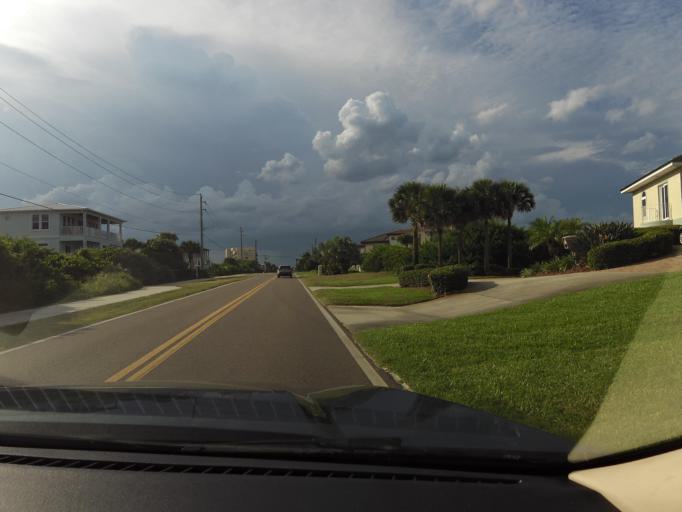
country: US
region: Florida
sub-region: Volusia County
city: Ponce Inlet
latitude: 29.0874
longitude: -80.9282
